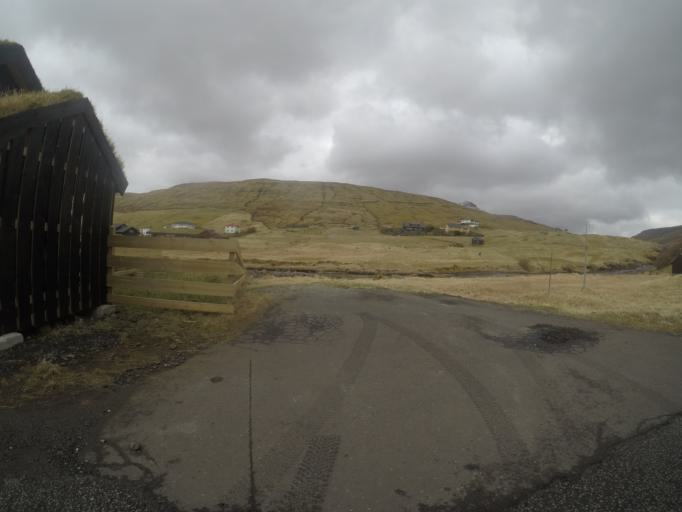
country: FO
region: Vagar
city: Midvagur
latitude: 62.0568
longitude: -7.1472
